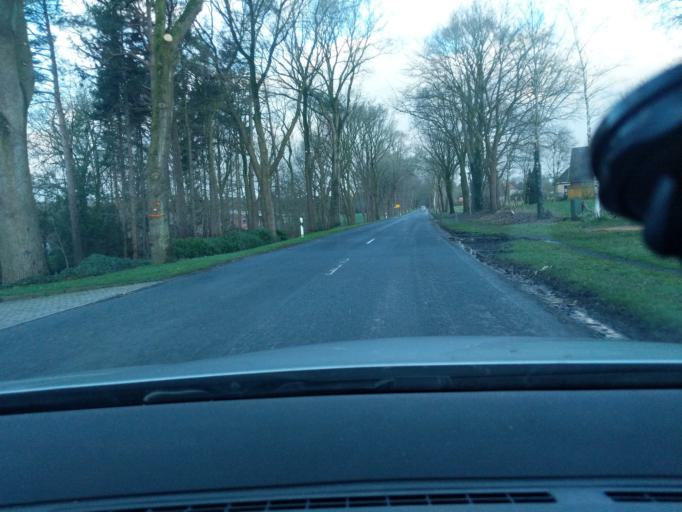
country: DE
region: Lower Saxony
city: Drangstedt
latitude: 53.6425
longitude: 8.7770
